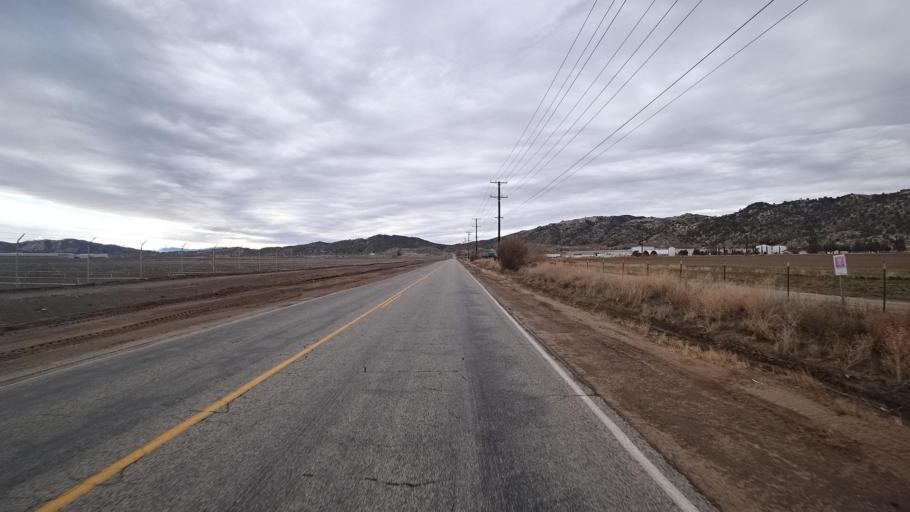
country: US
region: California
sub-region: Kern County
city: Bear Valley Springs
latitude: 35.1237
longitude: -118.5950
